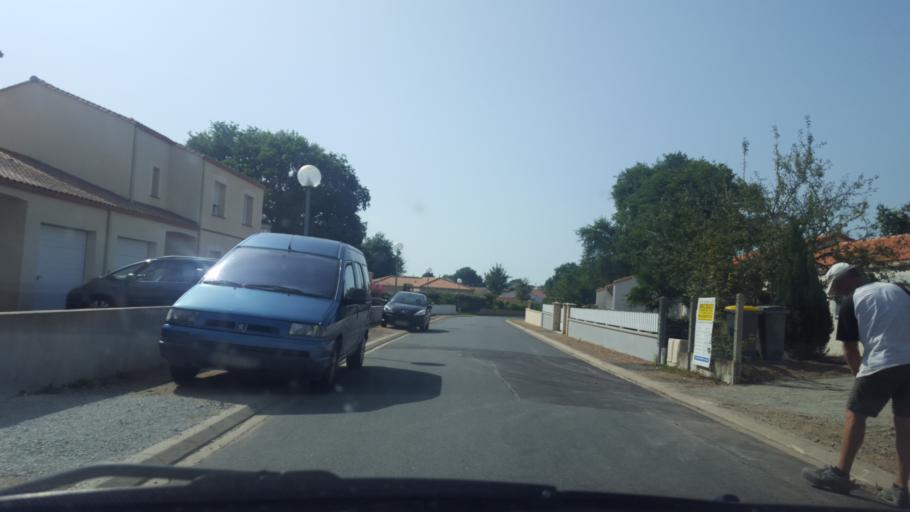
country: FR
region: Pays de la Loire
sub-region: Departement de la Loire-Atlantique
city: Saint-Philbert-de-Grand-Lieu
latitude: 47.0307
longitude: -1.6360
